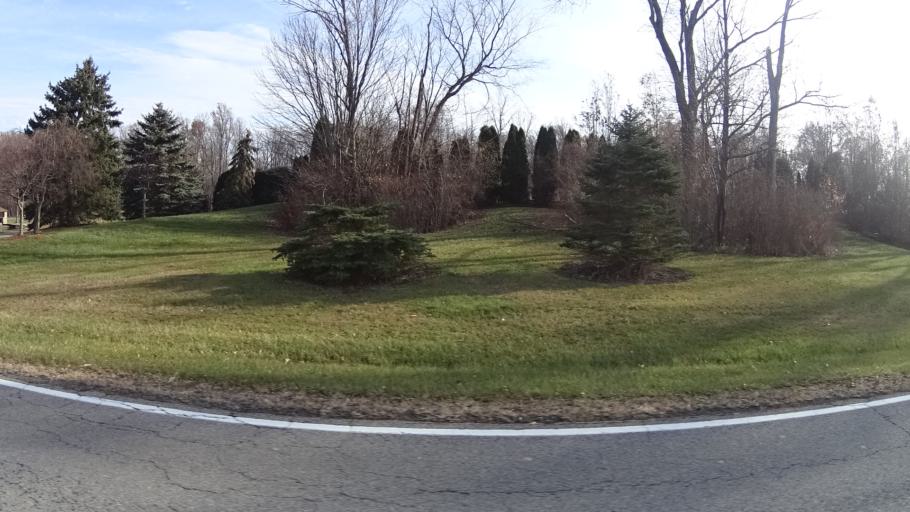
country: US
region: Ohio
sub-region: Lorain County
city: Grafton
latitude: 41.2311
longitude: -82.0427
